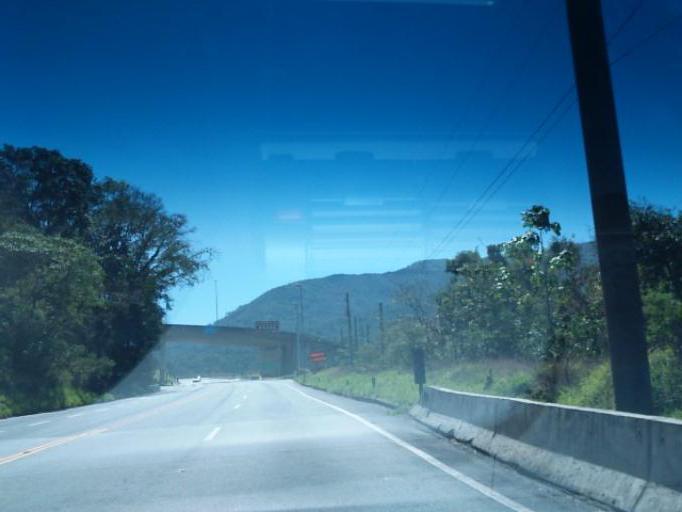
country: BR
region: Sao Paulo
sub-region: Campos Do Jordao
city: Campos do Jordao
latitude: -22.8332
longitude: -45.6241
